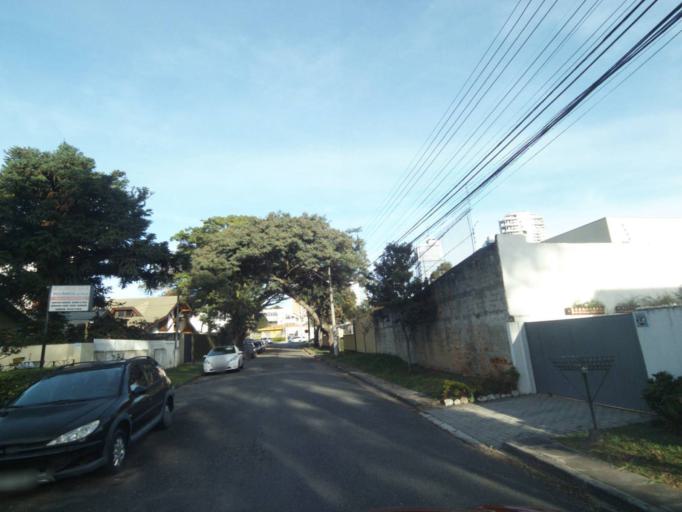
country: BR
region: Parana
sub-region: Curitiba
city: Curitiba
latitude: -25.4335
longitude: -49.3094
